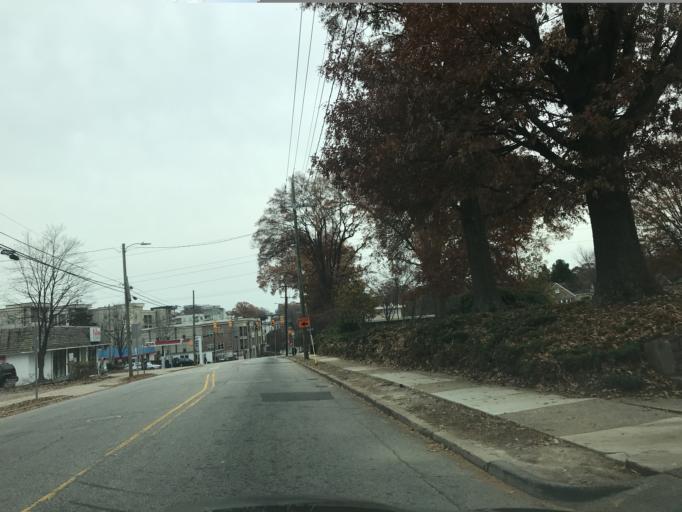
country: US
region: North Carolina
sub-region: Wake County
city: West Raleigh
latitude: 35.7896
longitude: -78.6512
